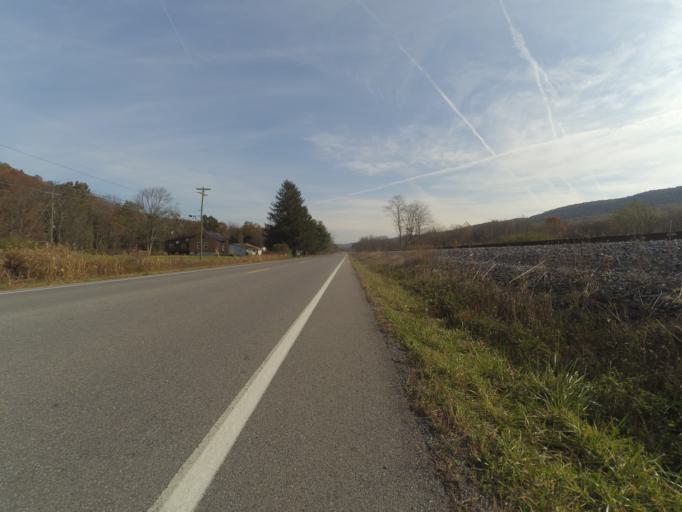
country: US
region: Pennsylvania
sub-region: Centre County
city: Stormstown
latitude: 40.8449
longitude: -77.9806
